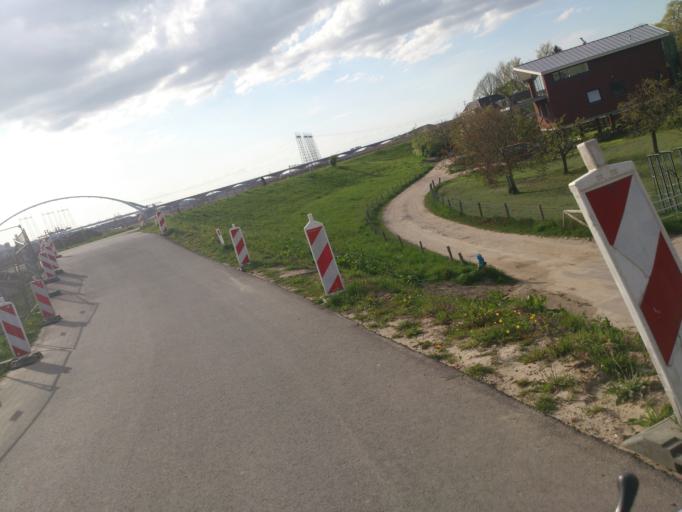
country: NL
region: Gelderland
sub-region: Gemeente Nijmegen
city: Nijmegen
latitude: 51.8569
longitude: 5.8580
